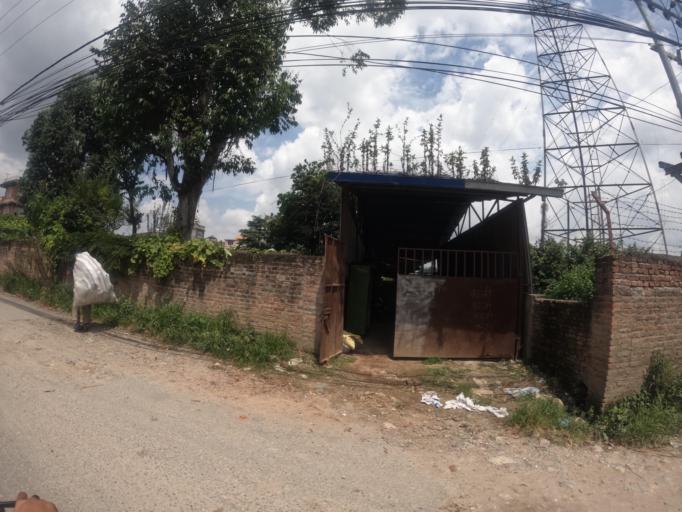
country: NP
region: Central Region
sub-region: Bagmati Zone
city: Bhaktapur
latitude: 27.6769
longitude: 85.3762
